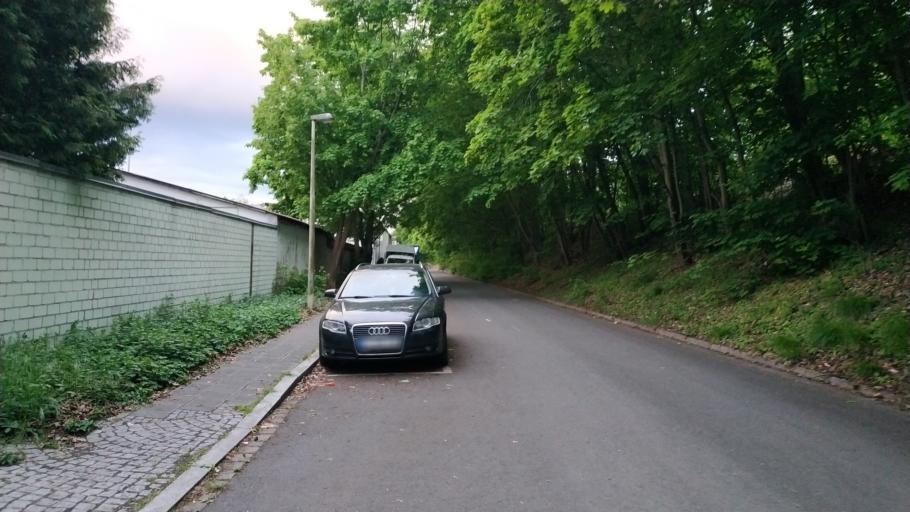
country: DE
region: Bavaria
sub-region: Regierungsbezirk Mittelfranken
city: Grossreuth bei Schweinau
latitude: 49.4258
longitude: 11.0551
